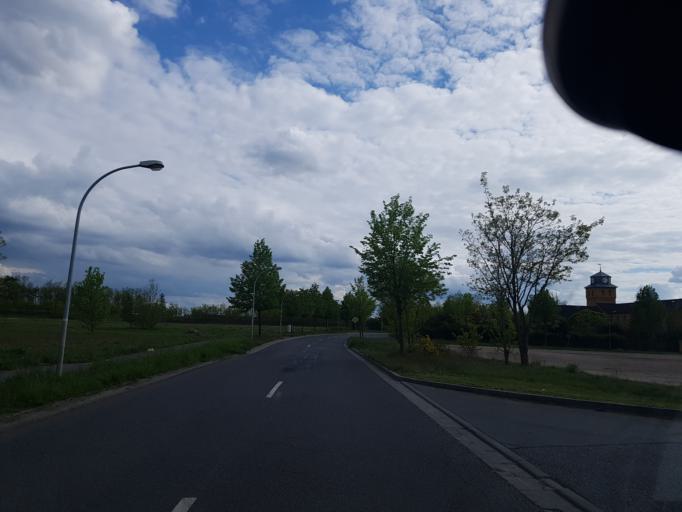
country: DE
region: Brandenburg
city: Grossraschen
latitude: 51.5804
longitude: 13.9802
